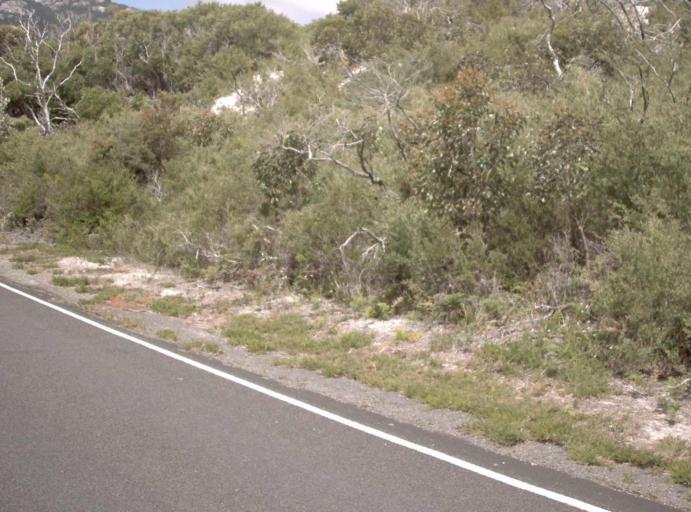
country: AU
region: Victoria
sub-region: Latrobe
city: Morwell
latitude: -39.0214
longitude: 146.3182
